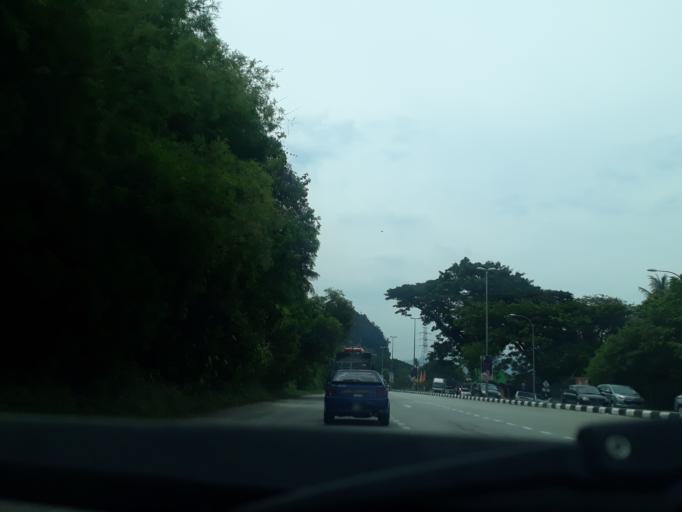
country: MY
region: Perak
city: Ipoh
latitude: 4.6378
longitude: 101.1548
